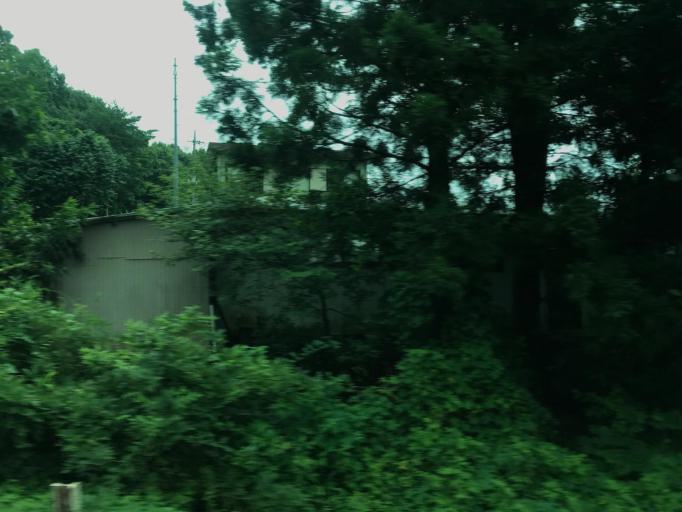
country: JP
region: Tochigi
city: Kuroiso
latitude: 37.0047
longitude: 140.0907
